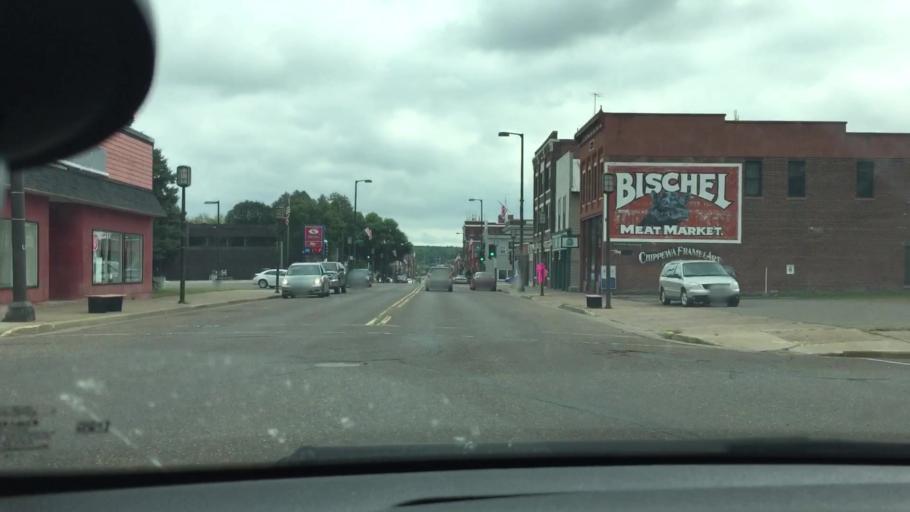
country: US
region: Wisconsin
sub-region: Chippewa County
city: Chippewa Falls
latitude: 44.9387
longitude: -91.3956
